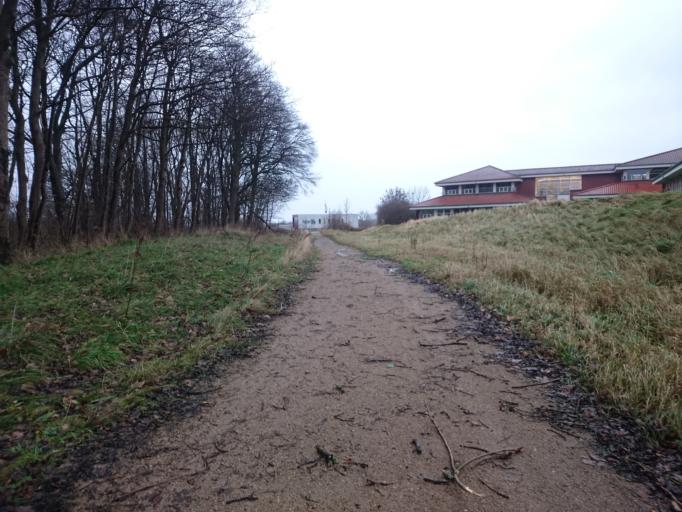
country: DK
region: Central Jutland
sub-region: Arhus Kommune
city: Stavtrup
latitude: 56.1152
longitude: 10.1291
